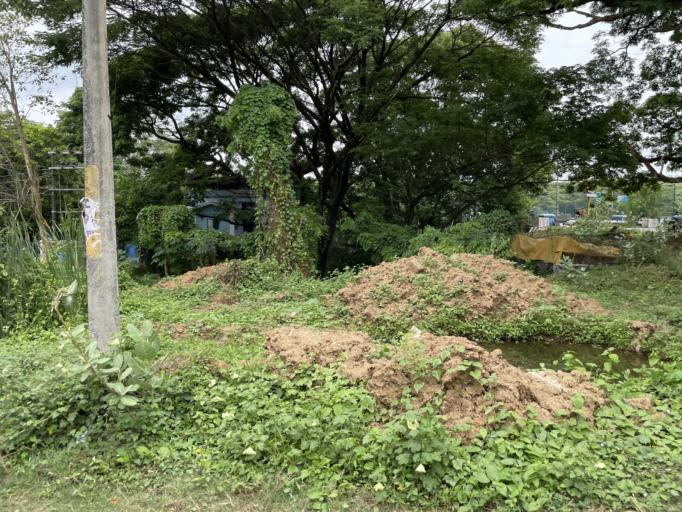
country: IN
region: Kerala
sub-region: Palakkad district
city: Chittur
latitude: 10.6885
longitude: 76.7178
